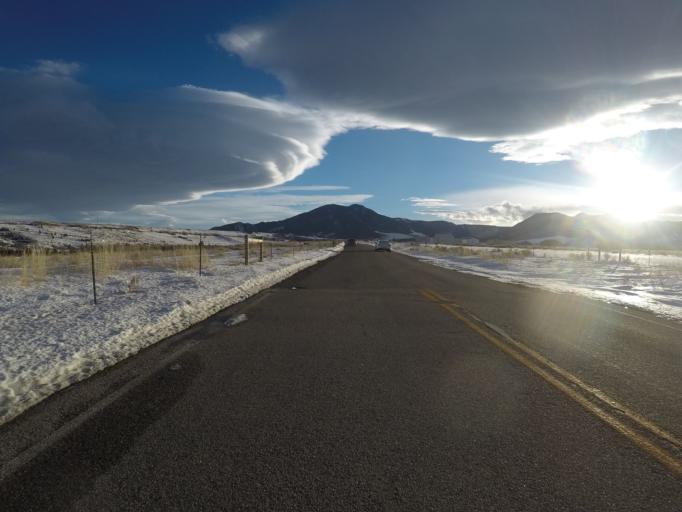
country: US
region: Montana
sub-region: Carbon County
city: Red Lodge
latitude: 45.1897
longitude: -109.2529
